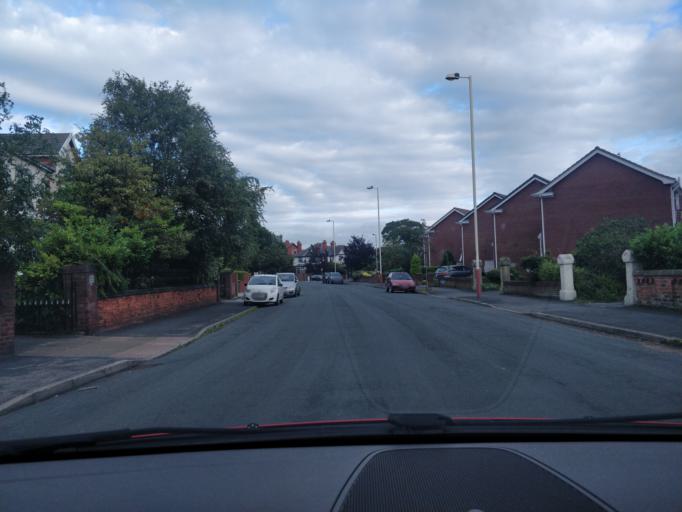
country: GB
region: England
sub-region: Sefton
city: Southport
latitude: 53.6517
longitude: -2.9851
